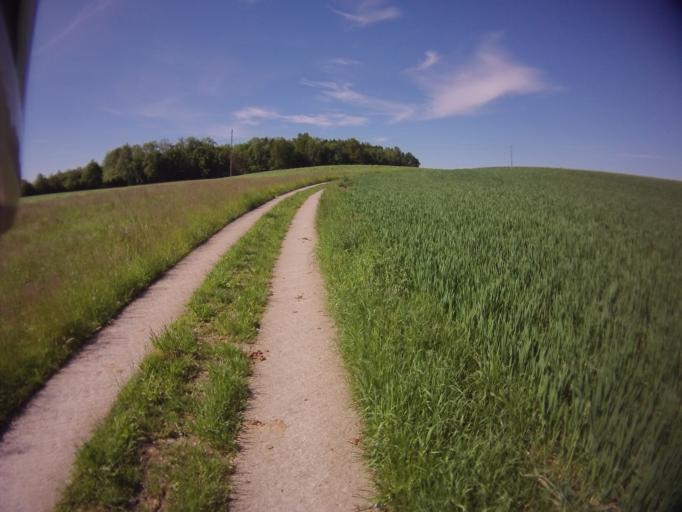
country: CH
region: Zug
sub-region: Zug
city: Cham
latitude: 47.2004
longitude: 8.4443
